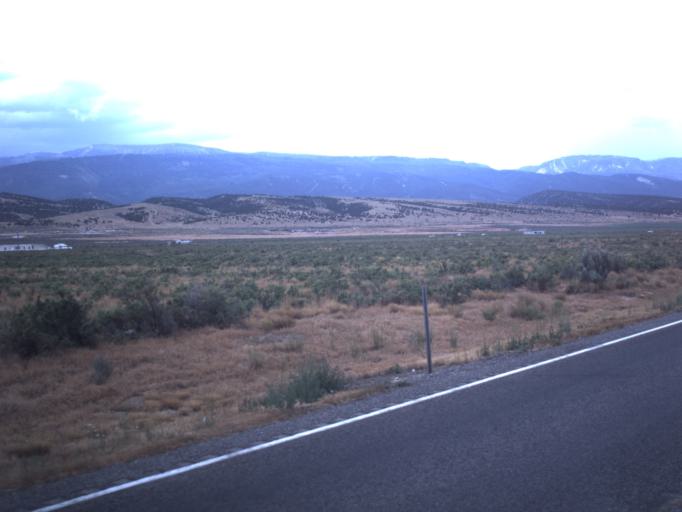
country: US
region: Utah
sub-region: Sanpete County
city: Moroni
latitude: 39.4573
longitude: -111.5626
